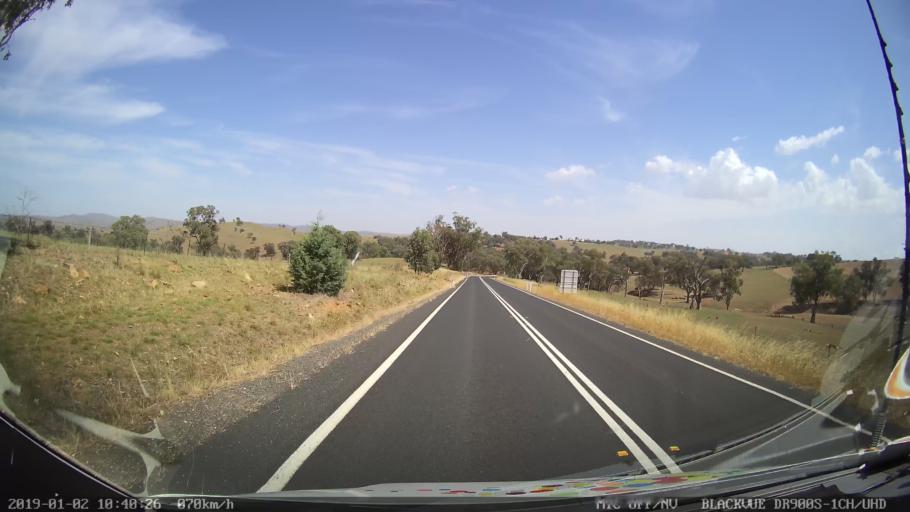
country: AU
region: New South Wales
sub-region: Cootamundra
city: Cootamundra
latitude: -34.8020
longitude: 148.3158
